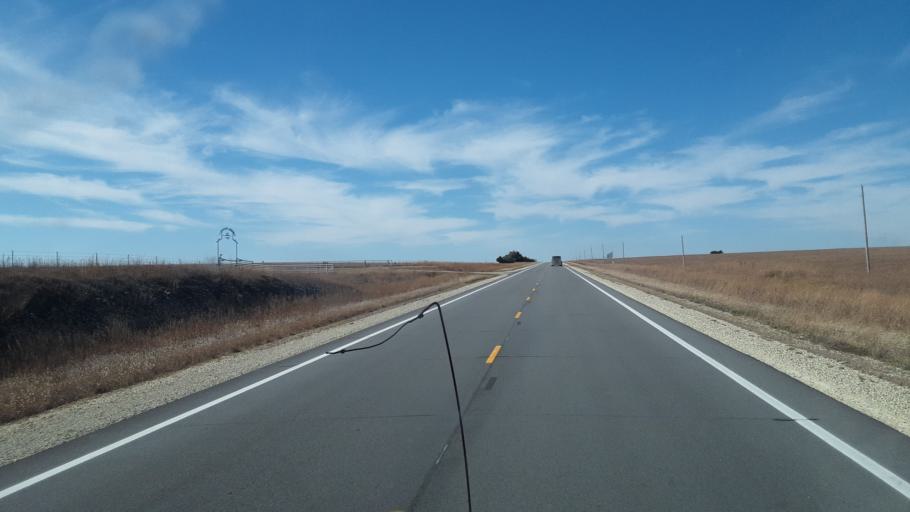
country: US
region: Kansas
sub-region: Marion County
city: Marion
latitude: 38.3628
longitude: -96.7898
